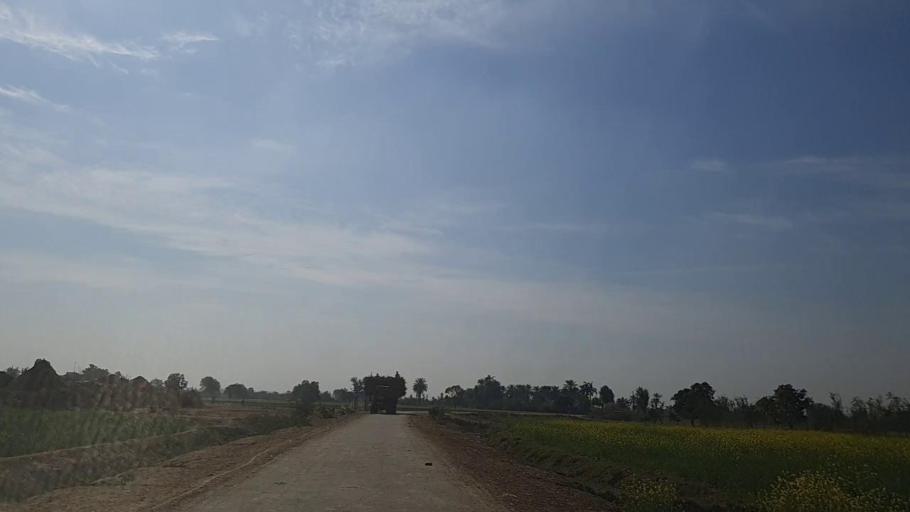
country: PK
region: Sindh
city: Mirpur Khas
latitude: 25.4712
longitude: 68.9645
